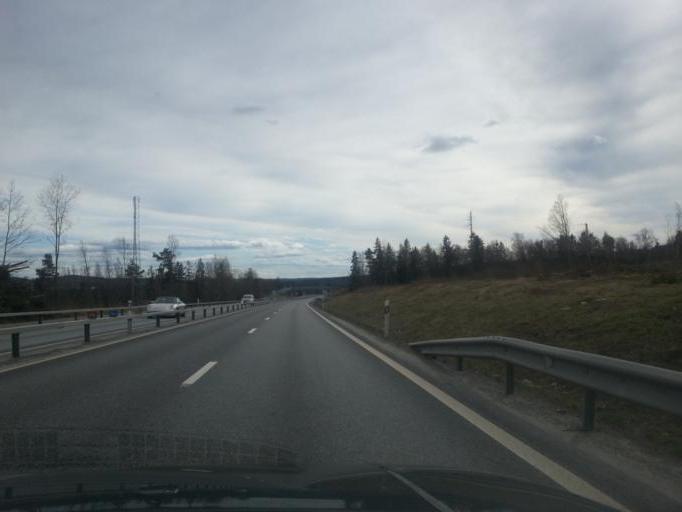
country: SE
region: Joenkoeping
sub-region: Habo Kommun
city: Habo
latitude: 57.8944
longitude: 14.1052
